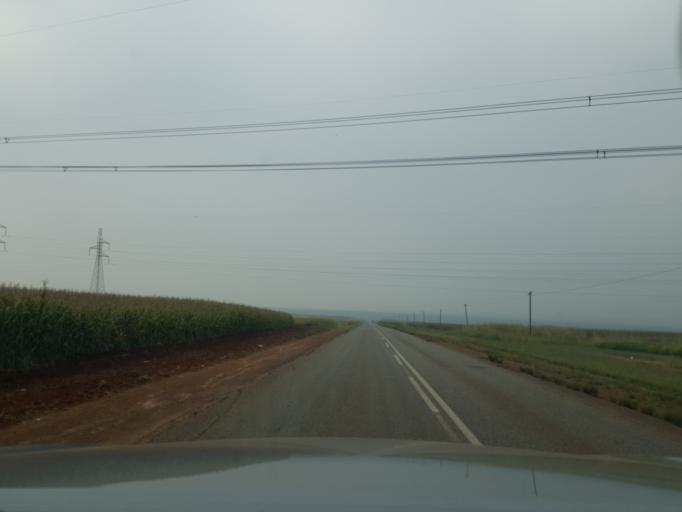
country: ZA
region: Mpumalanga
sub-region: Nkangala District Municipality
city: Middelburg
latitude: -26.0178
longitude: 29.4493
